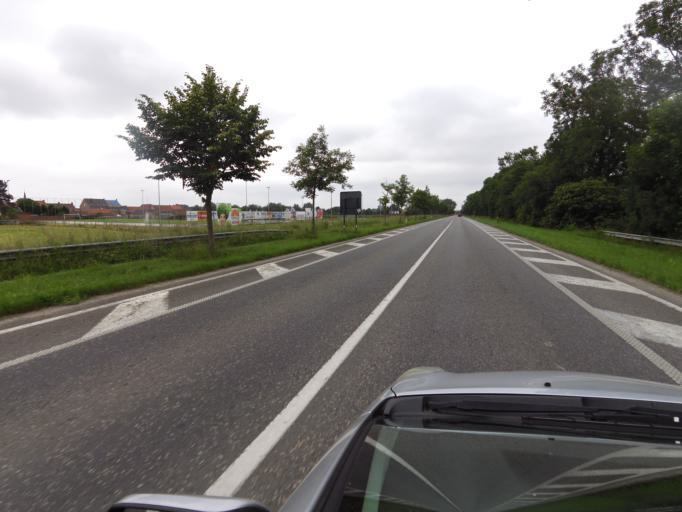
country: BE
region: Flanders
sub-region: Provincie West-Vlaanderen
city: Ieper
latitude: 50.8973
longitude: 2.8599
